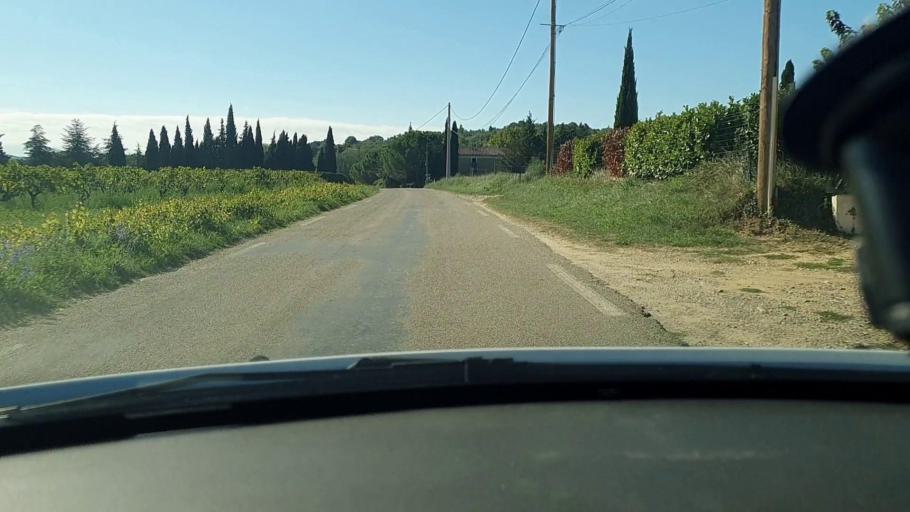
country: FR
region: Languedoc-Roussillon
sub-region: Departement du Gard
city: Saint-Julien-de-Peyrolas
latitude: 44.2830
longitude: 4.5717
